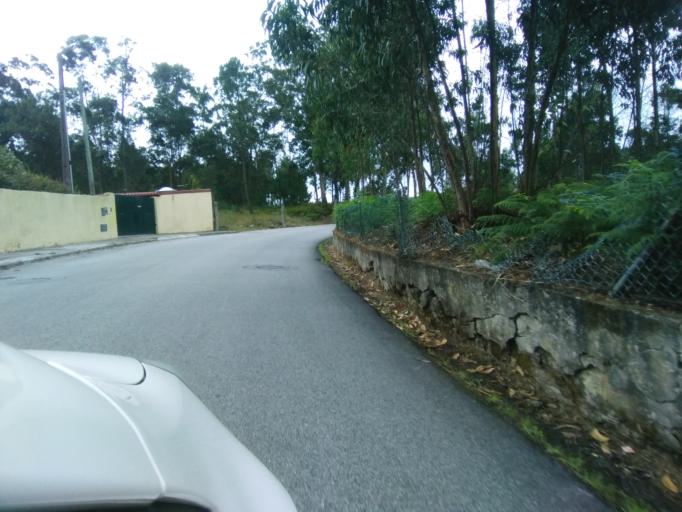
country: PT
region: Porto
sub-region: Matosinhos
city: Lavra
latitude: 41.2458
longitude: -8.7161
